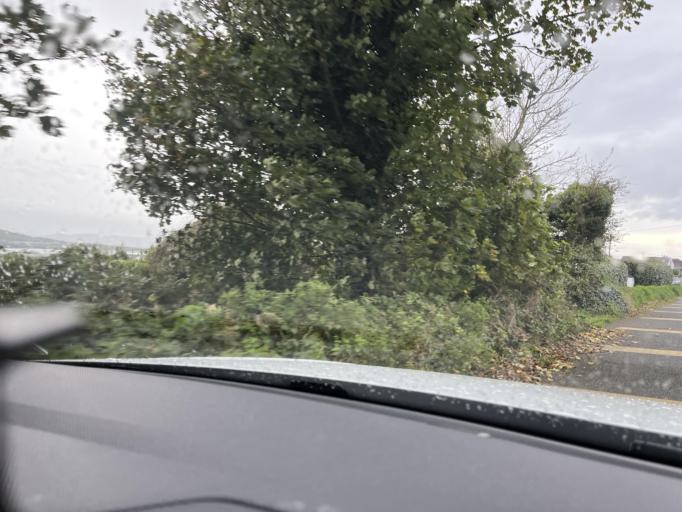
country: IE
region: Connaught
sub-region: Sligo
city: Strandhill
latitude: 54.3081
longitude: -8.5593
